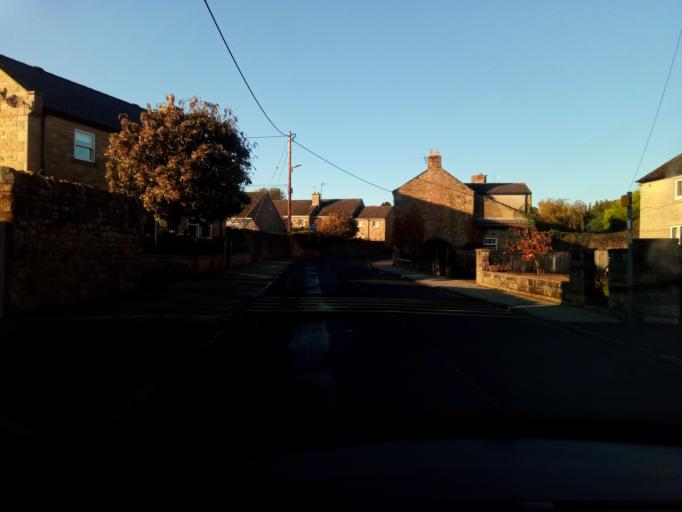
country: GB
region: England
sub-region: County Durham
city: Wolsingham
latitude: 54.7283
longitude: -1.8866
